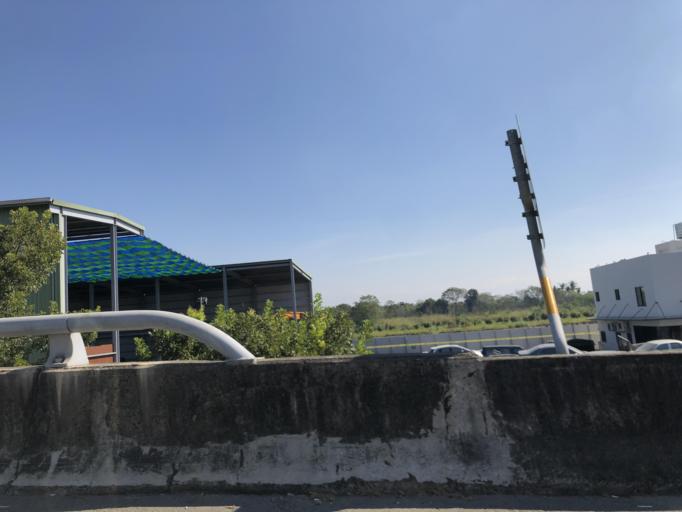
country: TW
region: Taiwan
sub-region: Tainan
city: Tainan
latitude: 23.0151
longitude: 120.2884
